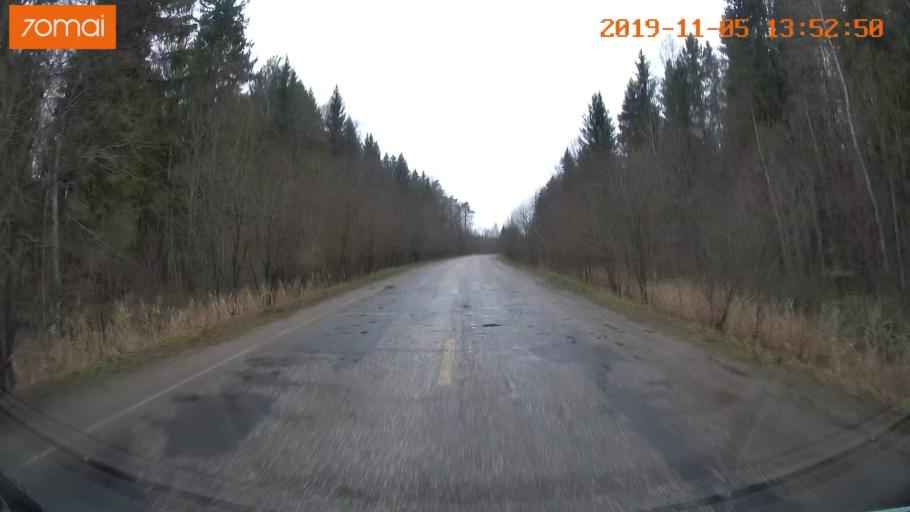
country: RU
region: Ivanovo
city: Kaminskiy
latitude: 57.0292
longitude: 41.3803
